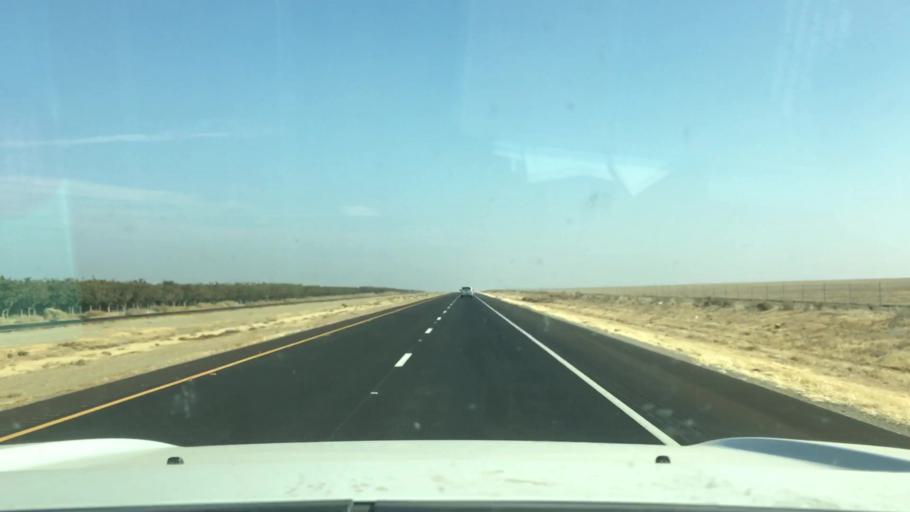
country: US
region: California
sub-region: Kern County
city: Lost Hills
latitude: 35.6143
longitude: -119.9456
